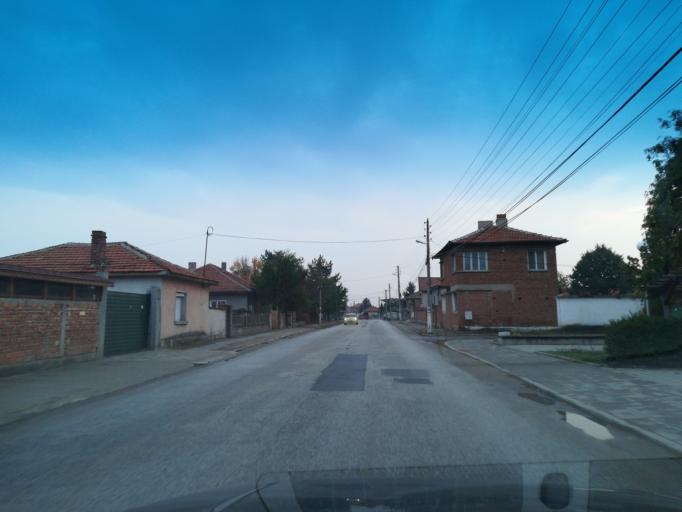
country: BG
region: Stara Zagora
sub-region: Obshtina Chirpan
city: Chirpan
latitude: 42.1751
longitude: 25.2094
